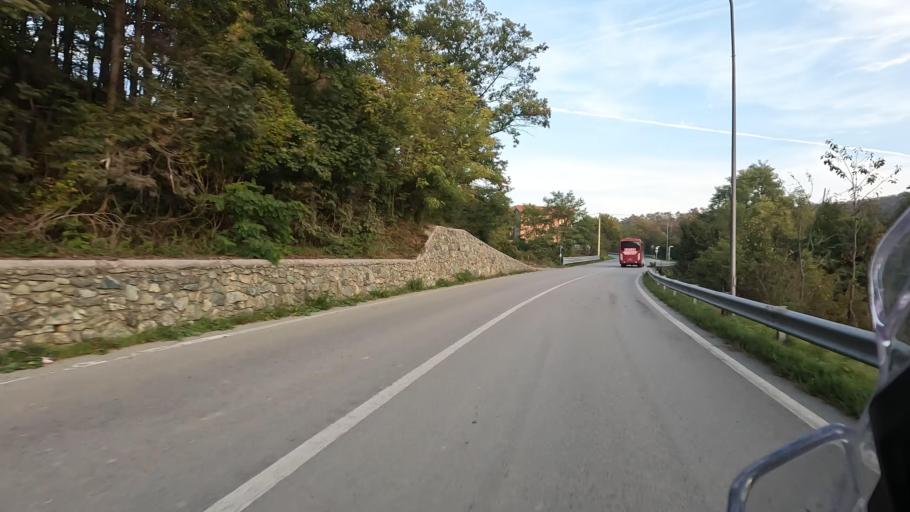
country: IT
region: Liguria
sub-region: Provincia di Savona
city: Pontinvrea
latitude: 44.4384
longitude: 8.4439
